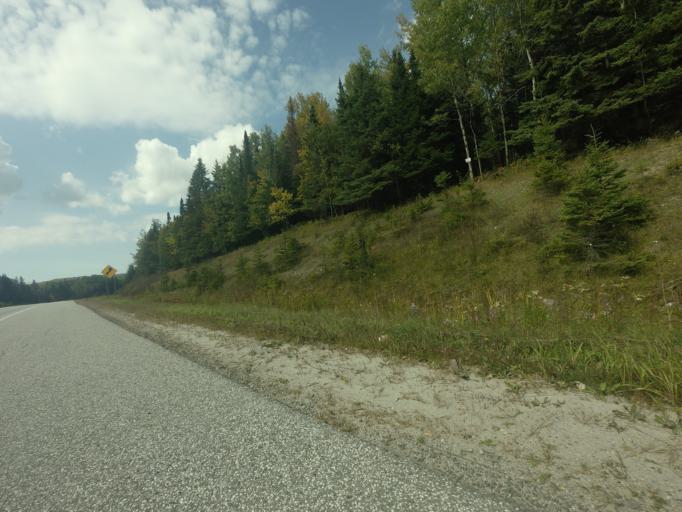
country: CA
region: Quebec
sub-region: Laurentides
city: Mont-Laurier
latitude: 46.5588
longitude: -75.6419
